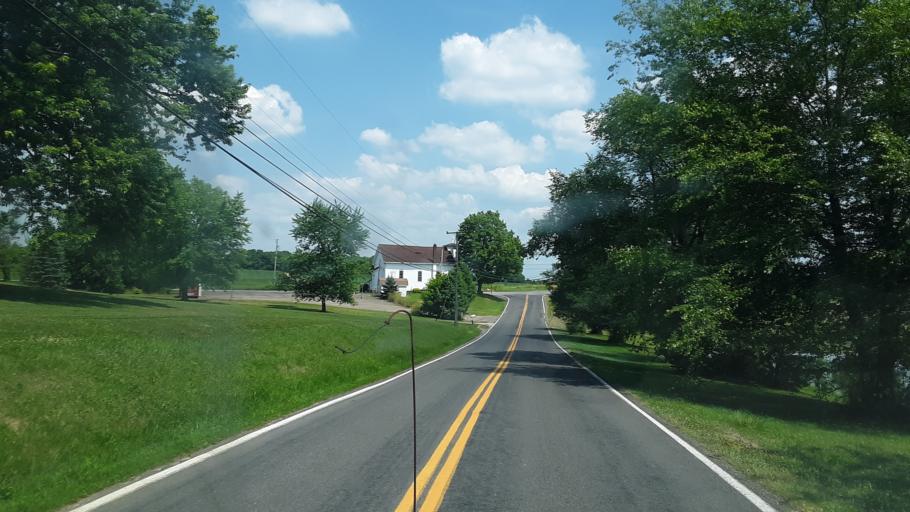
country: US
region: Ohio
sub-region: Stark County
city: Richville
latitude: 40.6954
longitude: -81.4729
